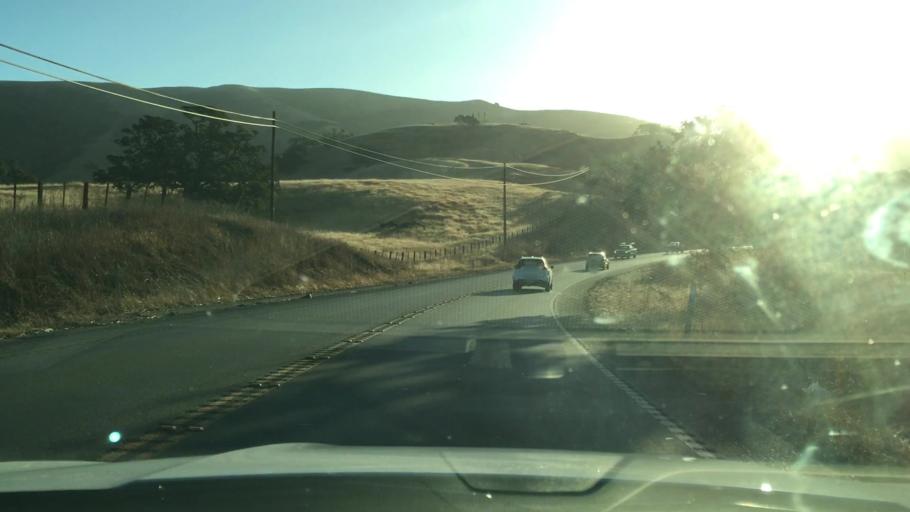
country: US
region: California
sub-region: Santa Clara County
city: Gilroy
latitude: 36.9891
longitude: -121.4508
